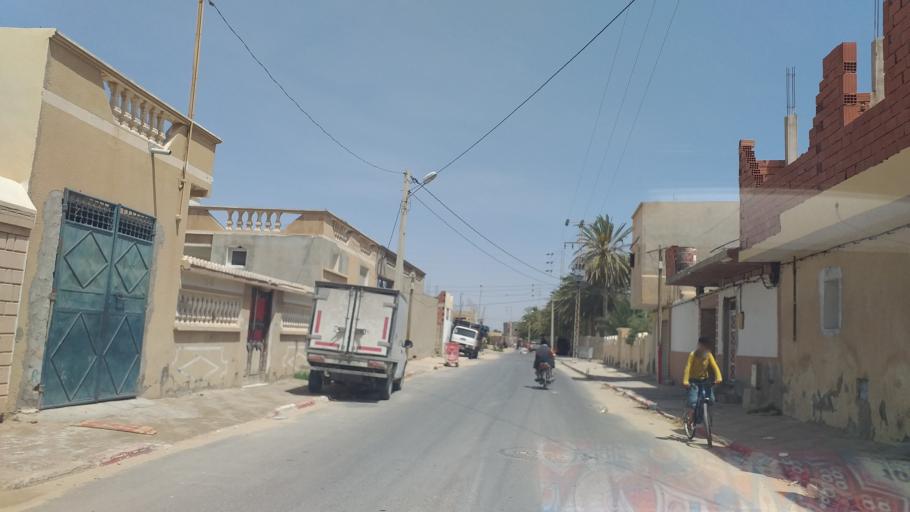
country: TN
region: Qabis
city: Gabes
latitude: 33.9456
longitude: 10.0617
